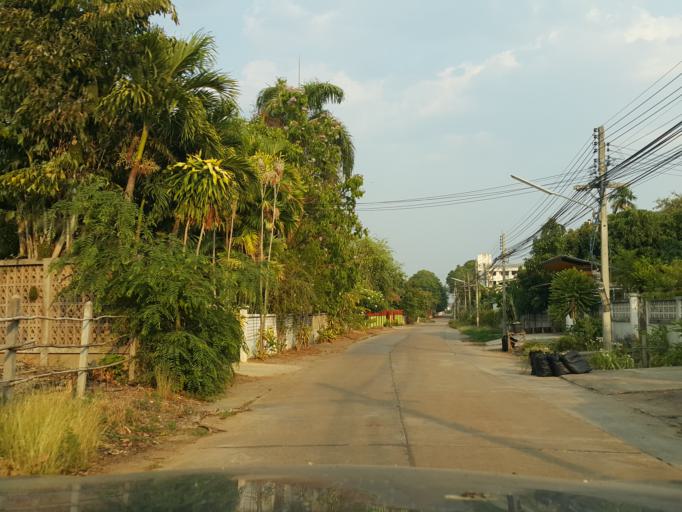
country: TH
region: Lamphun
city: Li
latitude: 17.8057
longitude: 98.9475
